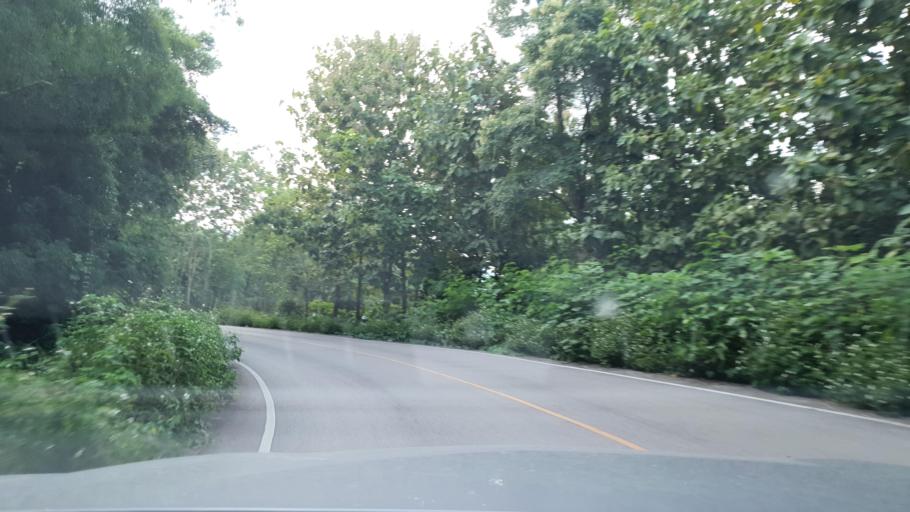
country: TH
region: Phayao
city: Phayao
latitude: 19.0977
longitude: 99.8311
